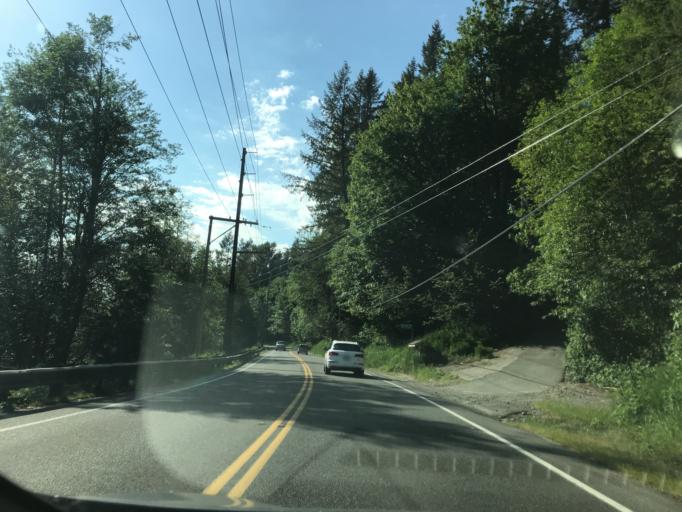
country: US
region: Washington
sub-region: King County
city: Mirrormont
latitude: 47.4607
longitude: -122.0082
